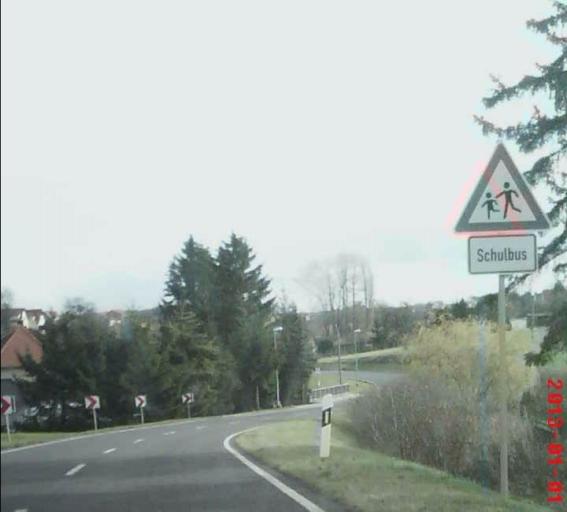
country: DE
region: Thuringia
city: Anrode
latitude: 51.2545
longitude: 10.3365
